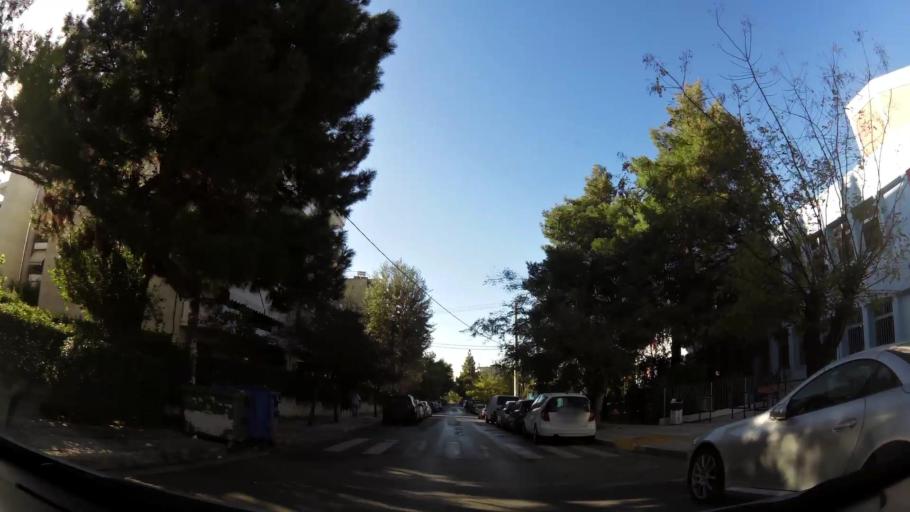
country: GR
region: Attica
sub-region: Nomarchia Athinas
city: Marousi
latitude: 38.0520
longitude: 23.7957
